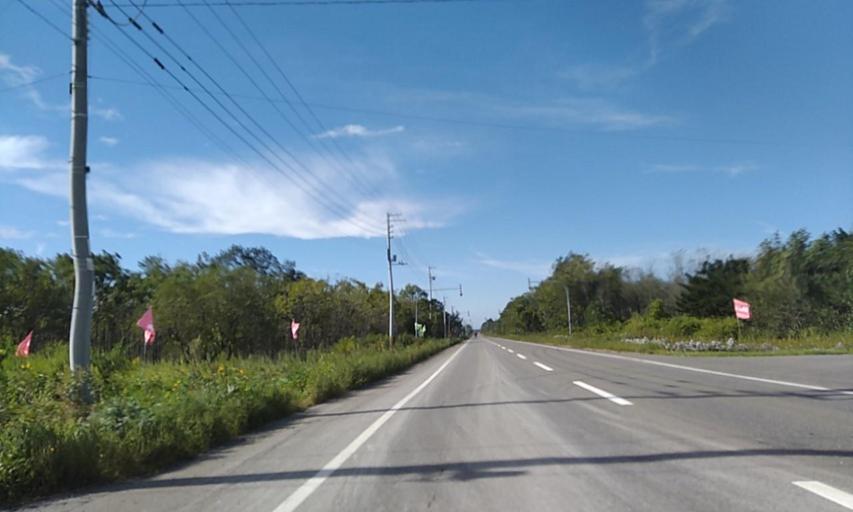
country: JP
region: Hokkaido
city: Obihiro
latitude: 42.7833
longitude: 143.5958
